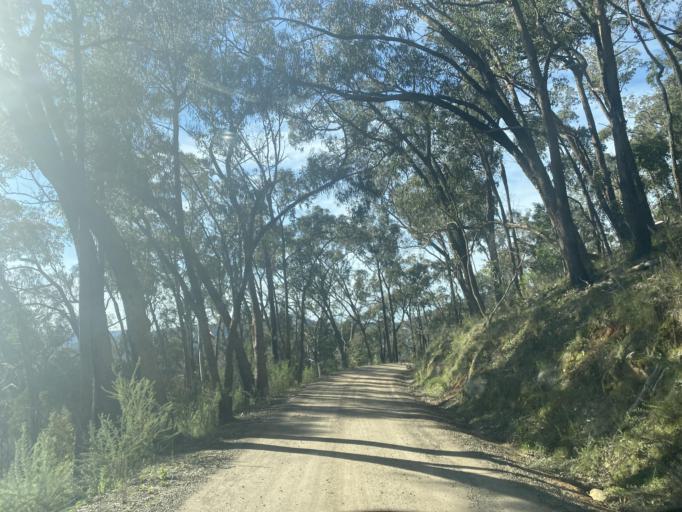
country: AU
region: Victoria
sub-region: Mansfield
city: Mansfield
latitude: -36.8394
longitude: 146.1648
